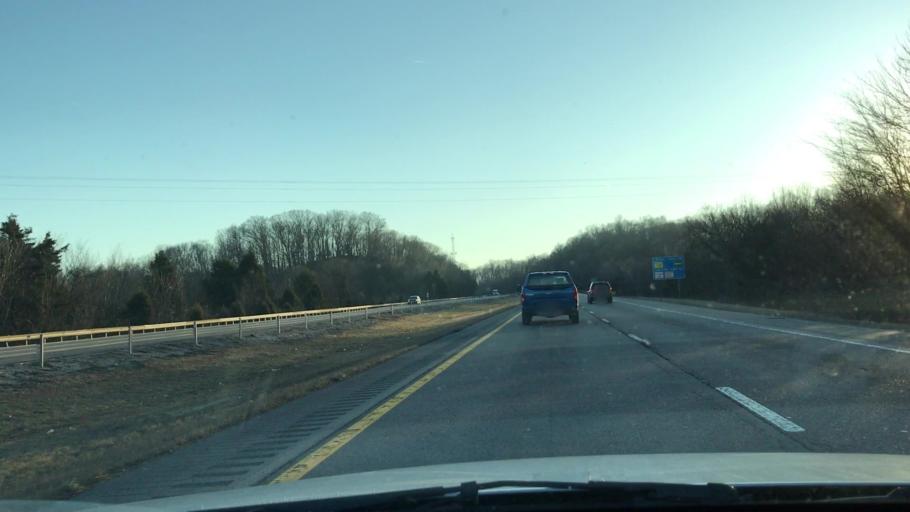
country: US
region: Tennessee
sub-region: Sumner County
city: Millersville
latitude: 36.3656
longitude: -86.7155
